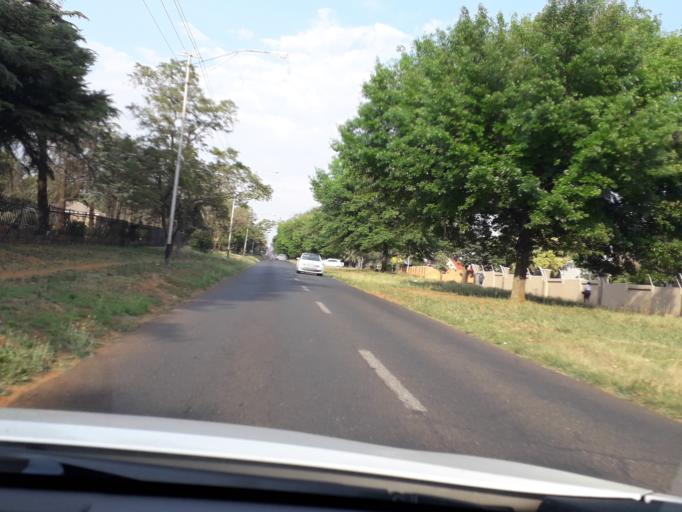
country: ZA
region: Gauteng
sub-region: City of Johannesburg Metropolitan Municipality
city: Johannesburg
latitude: -26.1612
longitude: 27.9873
